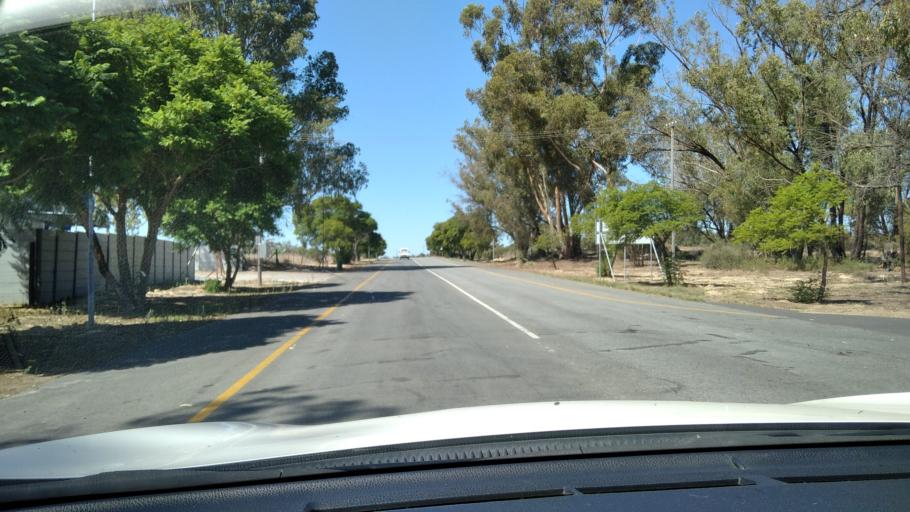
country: ZA
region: Western Cape
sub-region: West Coast District Municipality
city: Moorreesburg
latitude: -33.0633
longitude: 18.3534
